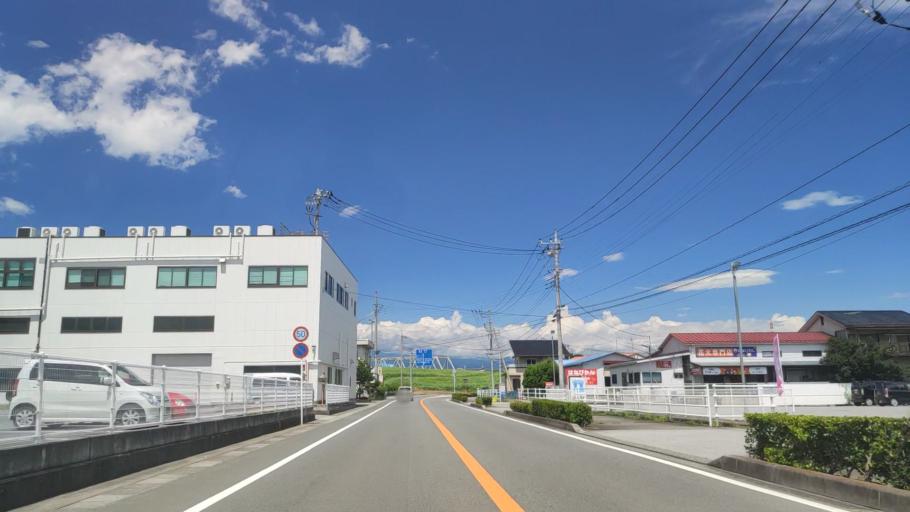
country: JP
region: Yamanashi
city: Ryuo
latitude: 35.5644
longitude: 138.4884
